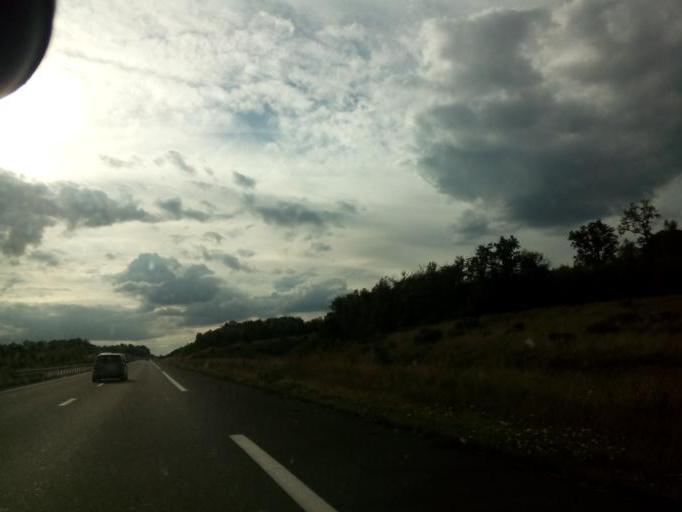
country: FR
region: Centre
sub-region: Departement du Loir-et-Cher
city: Thesee
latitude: 47.2922
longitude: 1.2846
